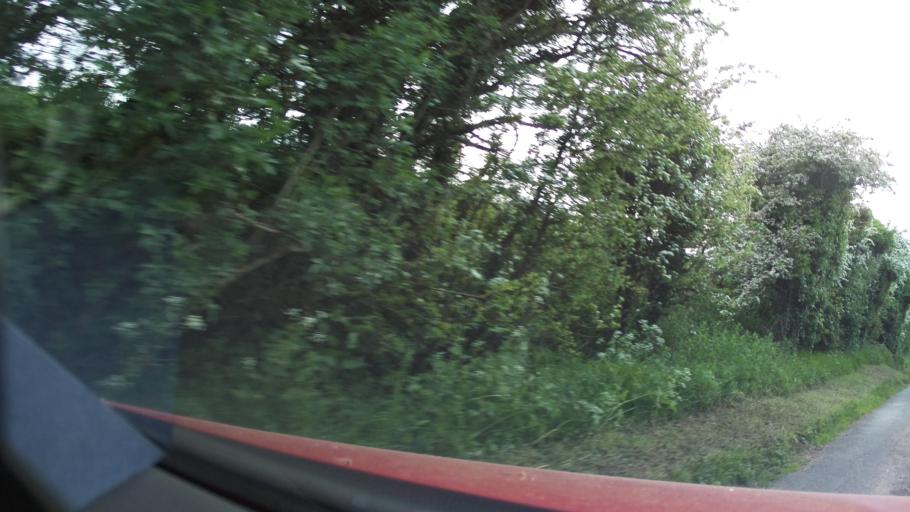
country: GB
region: England
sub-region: Gloucestershire
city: Shipton Village
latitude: 51.8771
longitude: -1.9368
